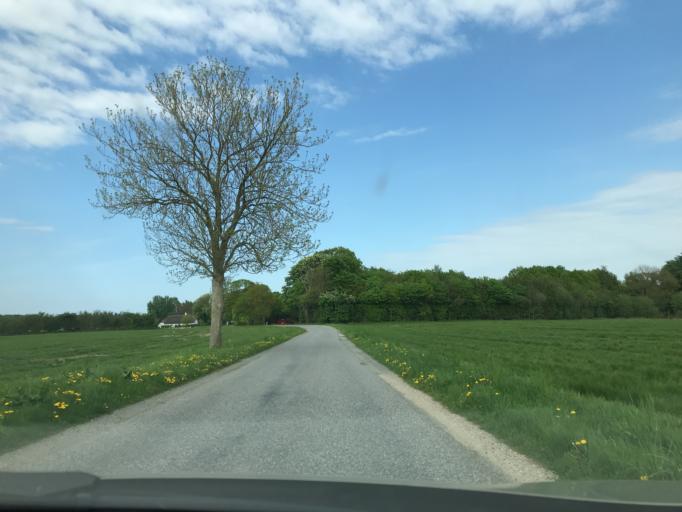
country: DK
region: South Denmark
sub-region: Middelfart Kommune
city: Norre Aby
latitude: 55.3981
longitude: 9.8607
